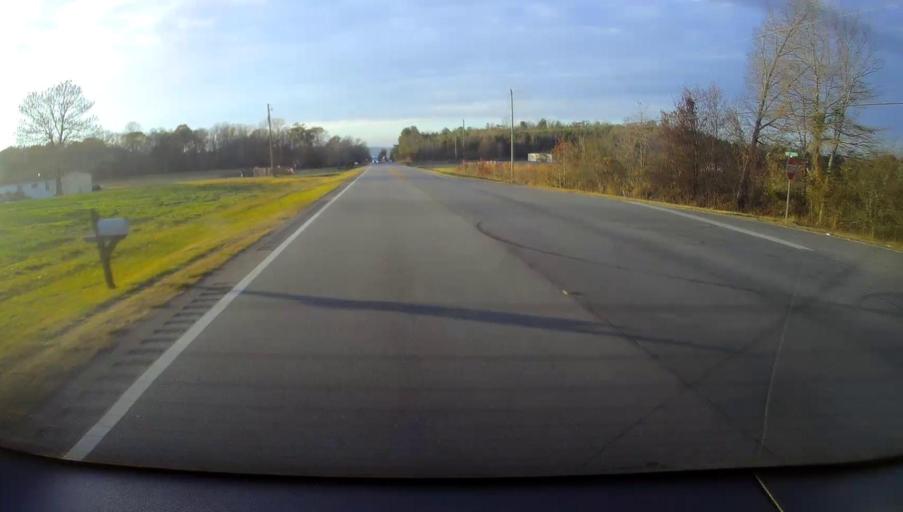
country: US
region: Alabama
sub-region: Saint Clair County
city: Steele
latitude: 34.0628
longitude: -86.2410
